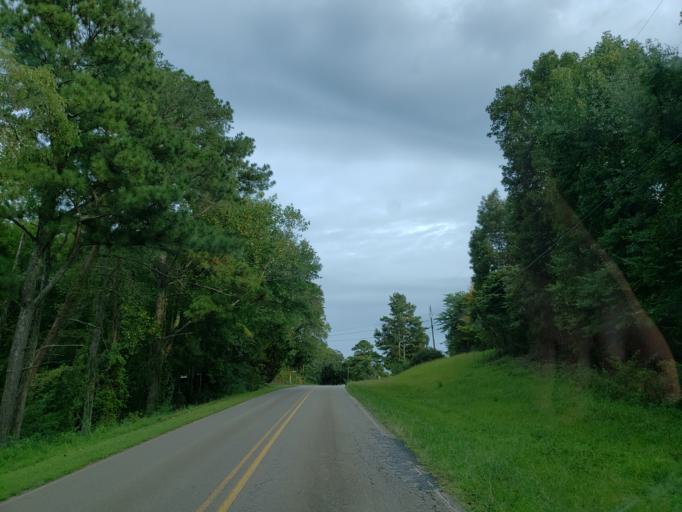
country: US
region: Georgia
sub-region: Pickens County
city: Jasper
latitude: 34.4971
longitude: -84.5184
